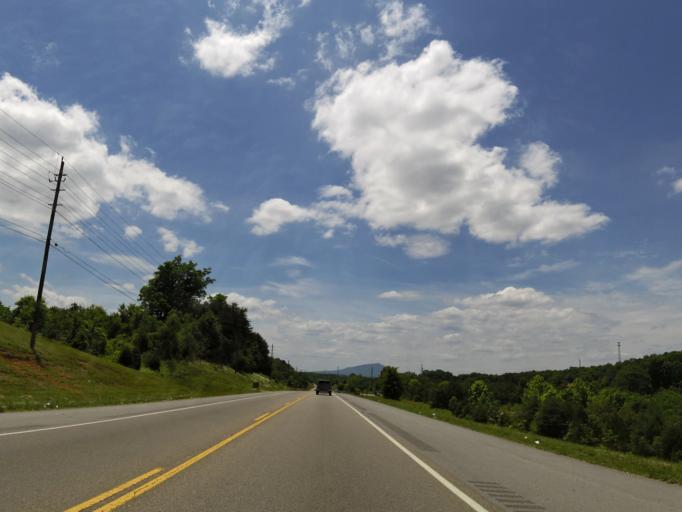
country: US
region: Tennessee
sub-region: Sevier County
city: Sevierville
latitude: 35.8723
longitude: -83.4938
